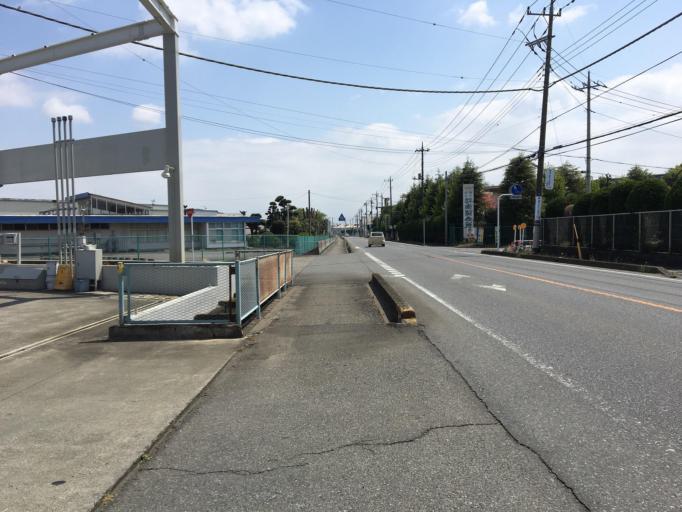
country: JP
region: Gunma
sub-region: Sawa-gun
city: Tamamura
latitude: 36.2952
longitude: 139.1393
